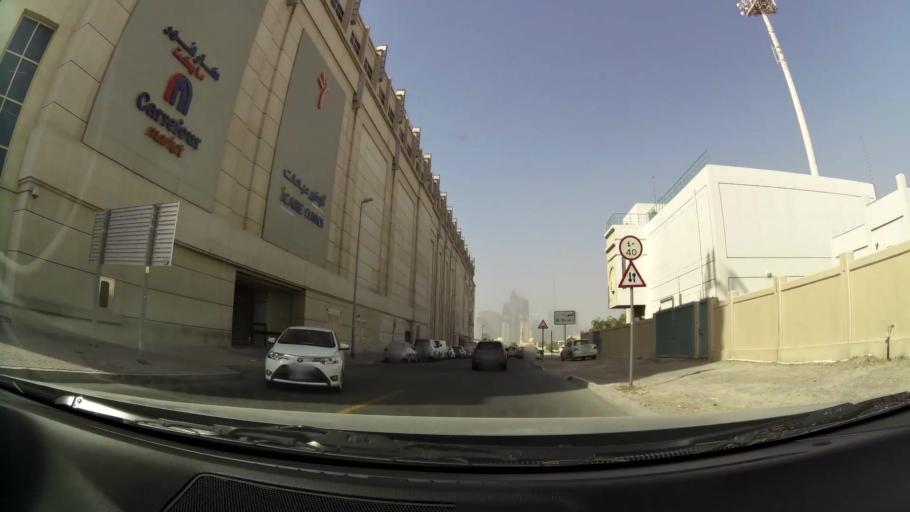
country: AE
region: Dubai
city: Dubai
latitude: 25.1685
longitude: 55.2418
